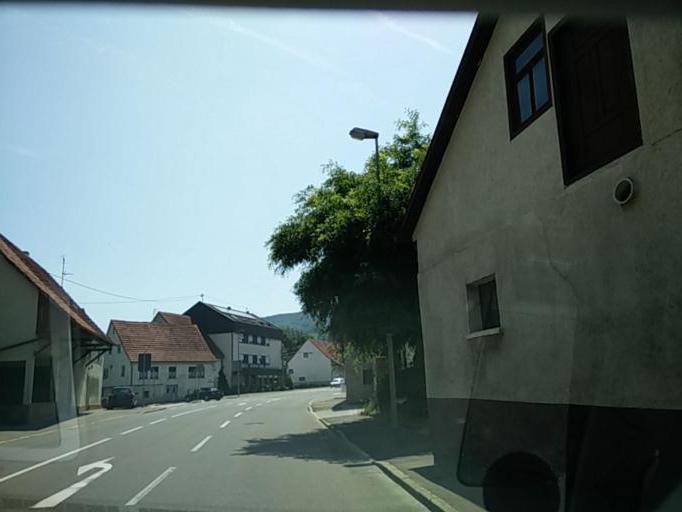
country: DE
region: Baden-Wuerttemberg
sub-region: Tuebingen Region
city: Gomaringen
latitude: 48.4500
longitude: 9.1386
